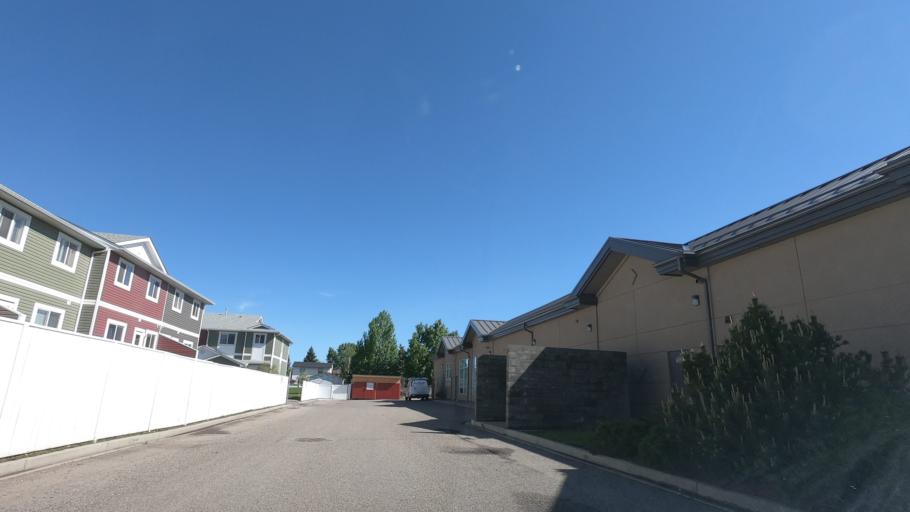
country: CA
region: Alberta
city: Airdrie
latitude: 51.2719
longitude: -113.9937
